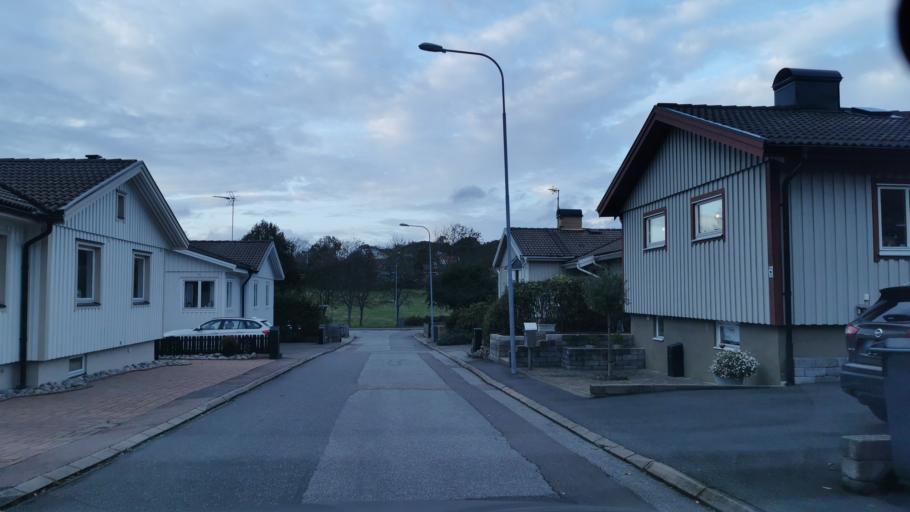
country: SE
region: Vaestra Goetaland
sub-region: Partille Kommun
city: Partille
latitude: 57.7222
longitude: 12.0865
